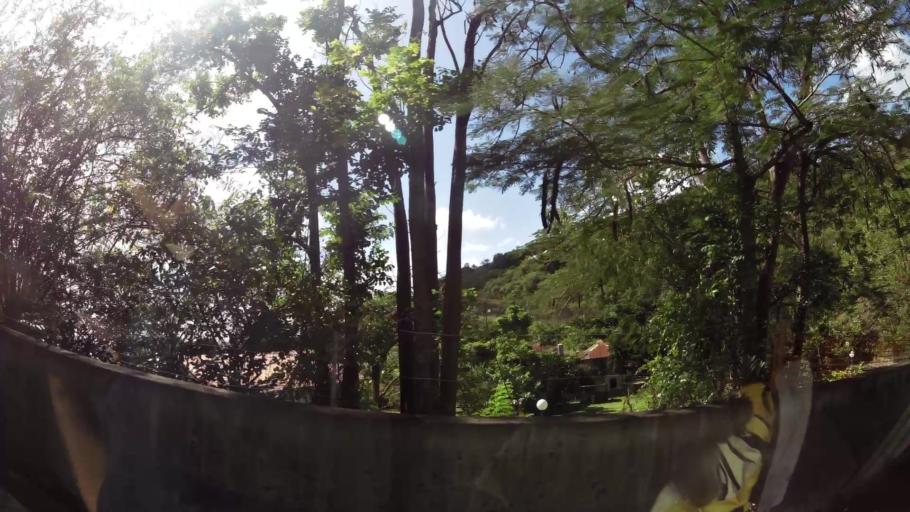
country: MQ
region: Martinique
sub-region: Martinique
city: Fort-de-France
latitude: 14.6312
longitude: -61.1193
